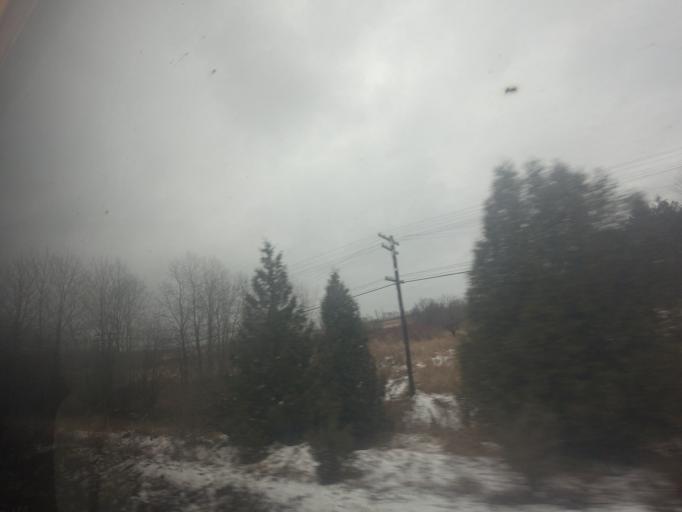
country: CA
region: Ontario
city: Cobourg
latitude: 43.9548
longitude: -78.2280
